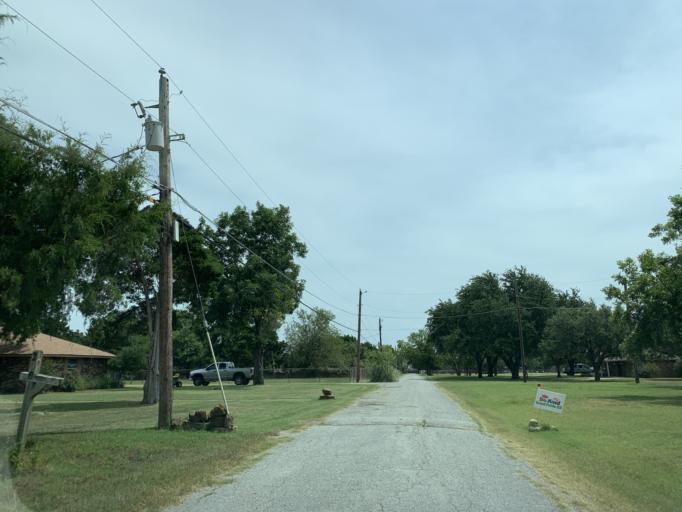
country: US
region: Texas
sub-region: Dallas County
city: Cedar Hill
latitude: 32.6537
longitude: -97.0033
